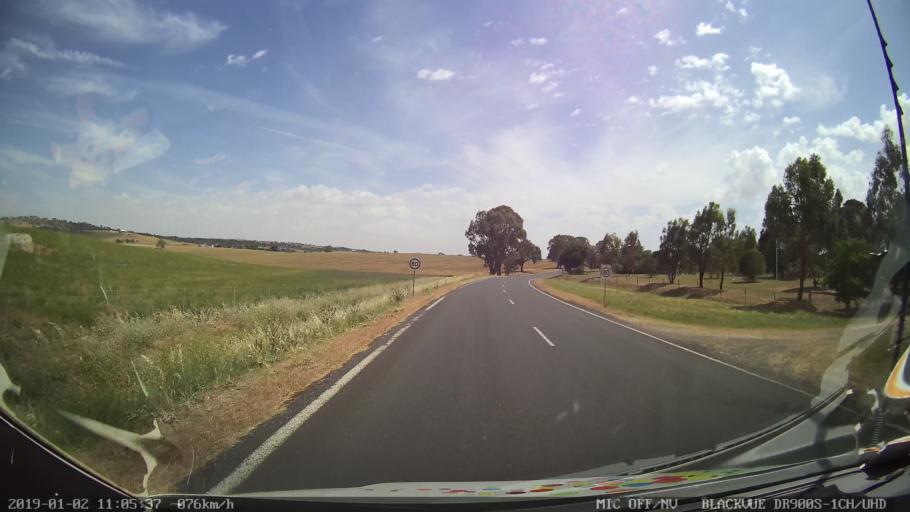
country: AU
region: New South Wales
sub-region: Young
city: Young
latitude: -34.5628
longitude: 148.3538
